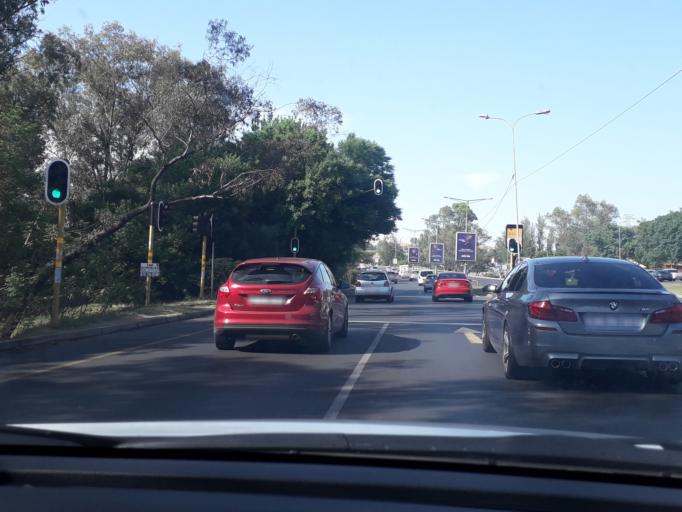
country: ZA
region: Gauteng
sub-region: City of Johannesburg Metropolitan Municipality
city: Diepsloot
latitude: -26.0313
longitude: 28.0275
